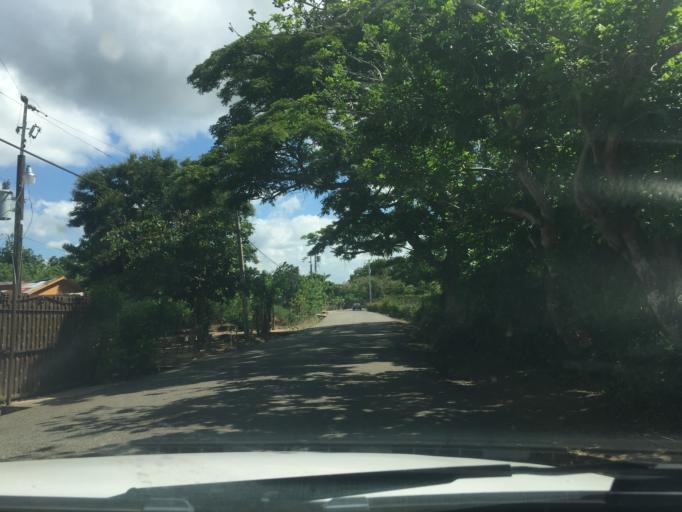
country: DO
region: La Vega
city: Rio Verde Arriba
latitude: 19.3643
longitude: -70.5964
